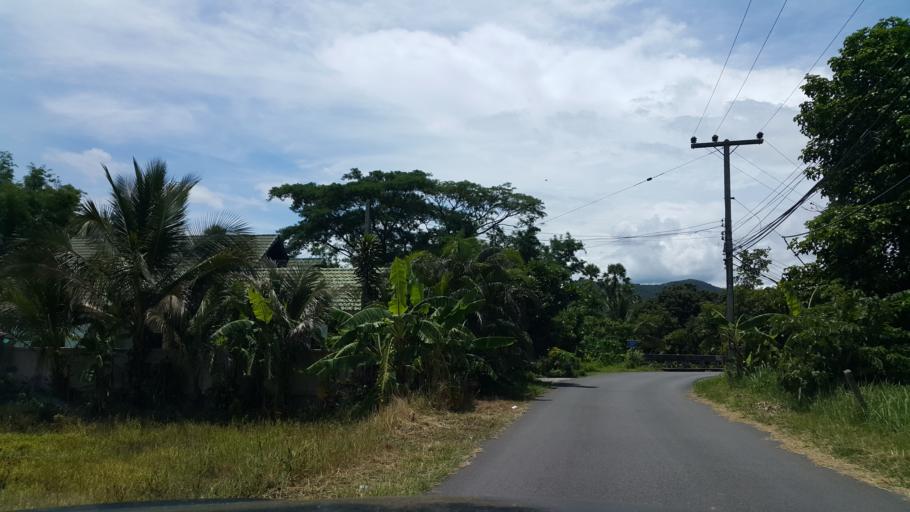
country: TH
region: Chiang Mai
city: Mae On
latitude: 18.7265
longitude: 99.2016
